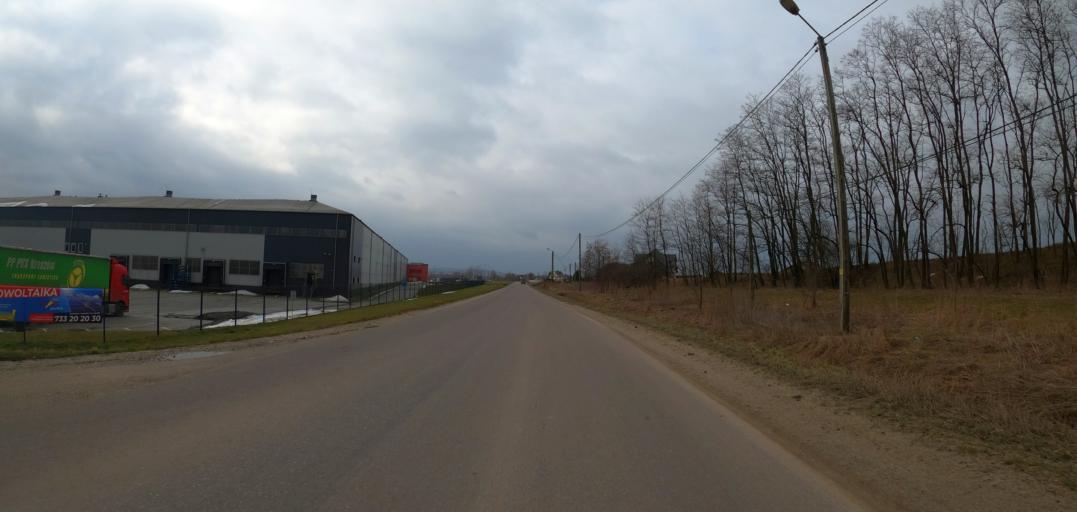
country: PL
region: Subcarpathian Voivodeship
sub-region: Powiat debicki
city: Pilzno
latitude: 49.9871
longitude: 21.3215
